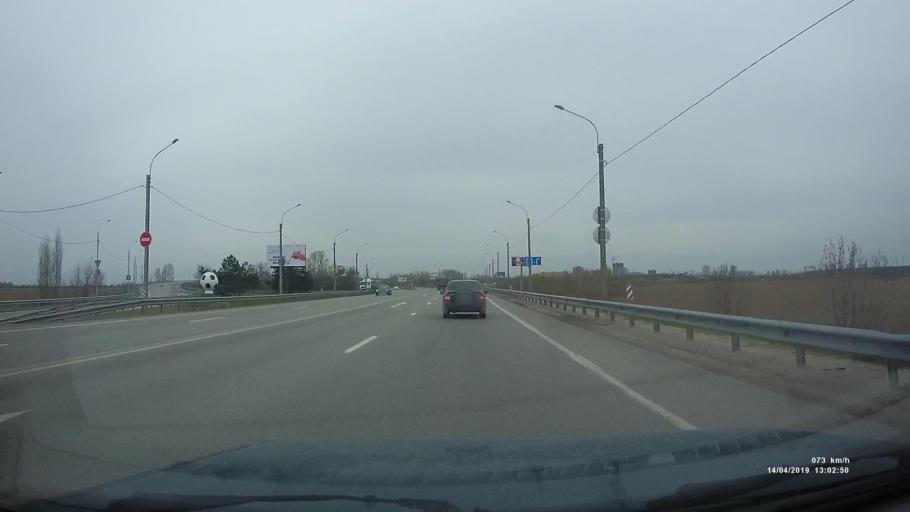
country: RU
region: Rostov
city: Bataysk
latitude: 47.1726
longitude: 39.7430
